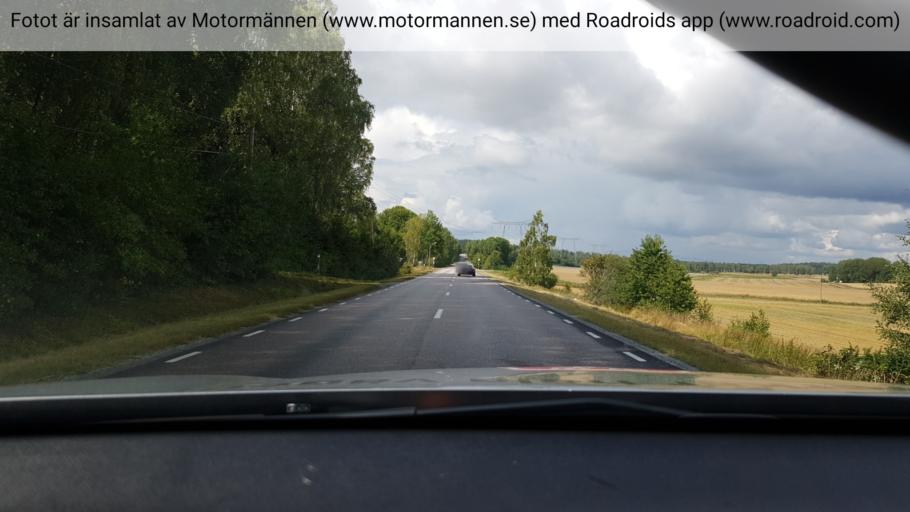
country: SE
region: Stockholm
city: Stenhamra
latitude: 59.3694
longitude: 17.6084
